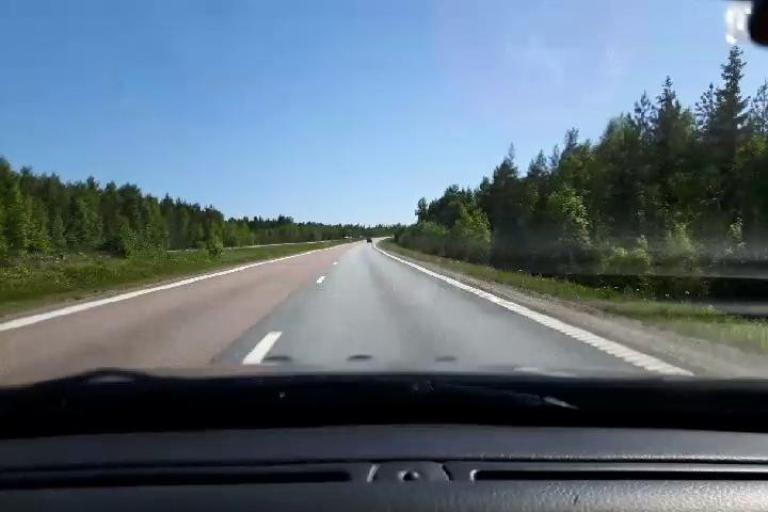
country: SE
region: Gaevleborg
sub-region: Soderhamns Kommun
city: Soderhamn
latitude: 61.4749
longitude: 16.9892
